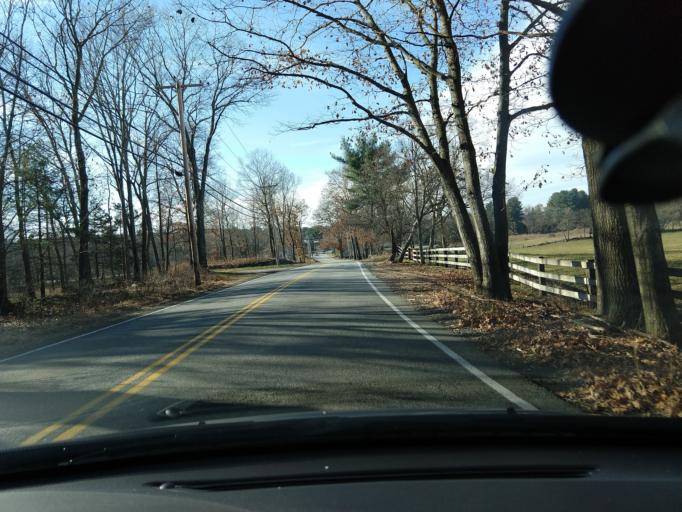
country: US
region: Massachusetts
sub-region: Middlesex County
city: Dunstable
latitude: 42.6751
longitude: -71.4702
